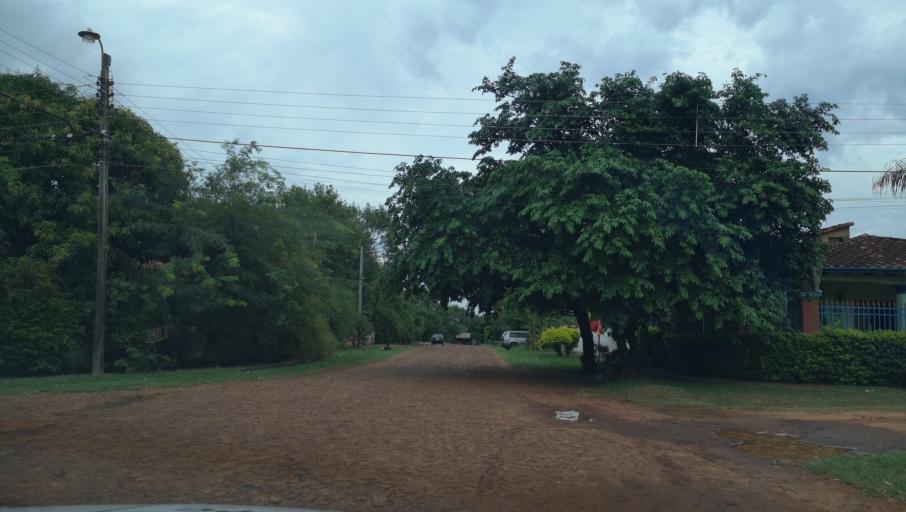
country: PY
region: Misiones
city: Santa Maria
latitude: -26.8885
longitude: -57.0435
